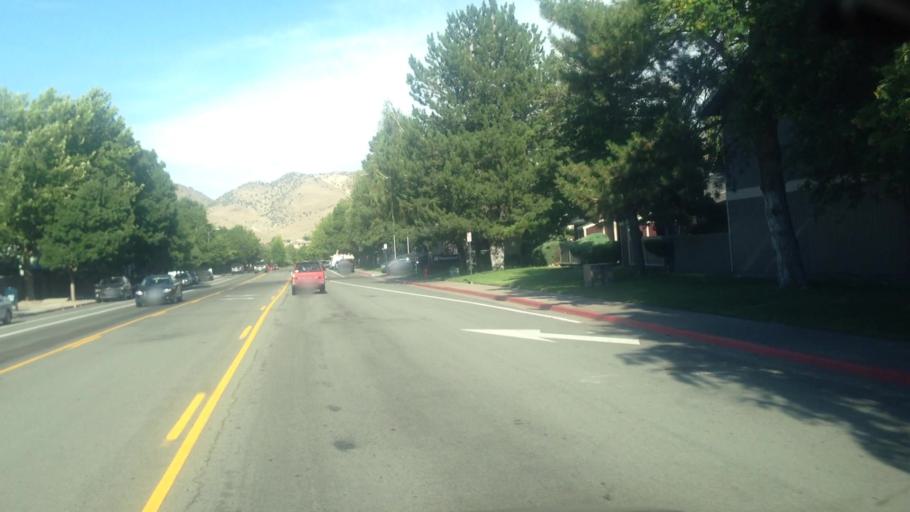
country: US
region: Nevada
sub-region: Washoe County
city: Sparks
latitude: 39.4861
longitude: -119.7456
